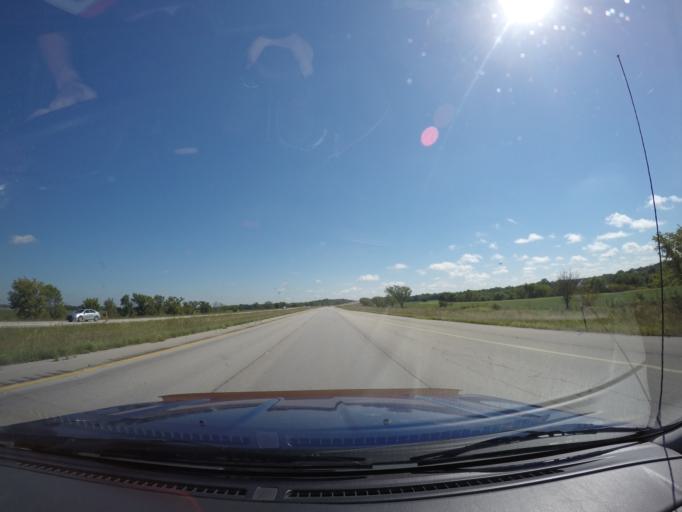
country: US
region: Kansas
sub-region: Douglas County
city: Eudora
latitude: 38.9348
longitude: -95.1443
